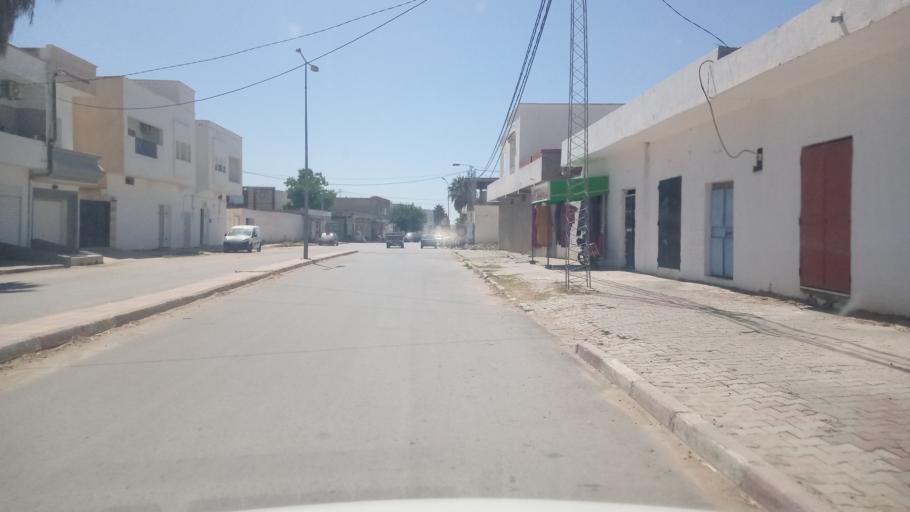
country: TN
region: Al Qayrawan
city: Sbikha
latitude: 36.1198
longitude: 10.0908
